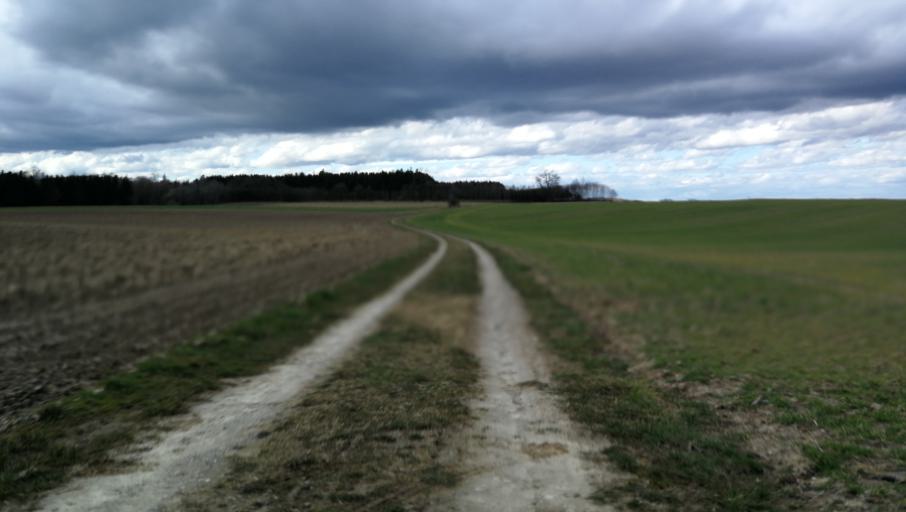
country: DE
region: Bavaria
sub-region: Upper Bavaria
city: Fuerstenfeldbruck
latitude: 48.1948
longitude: 11.2121
